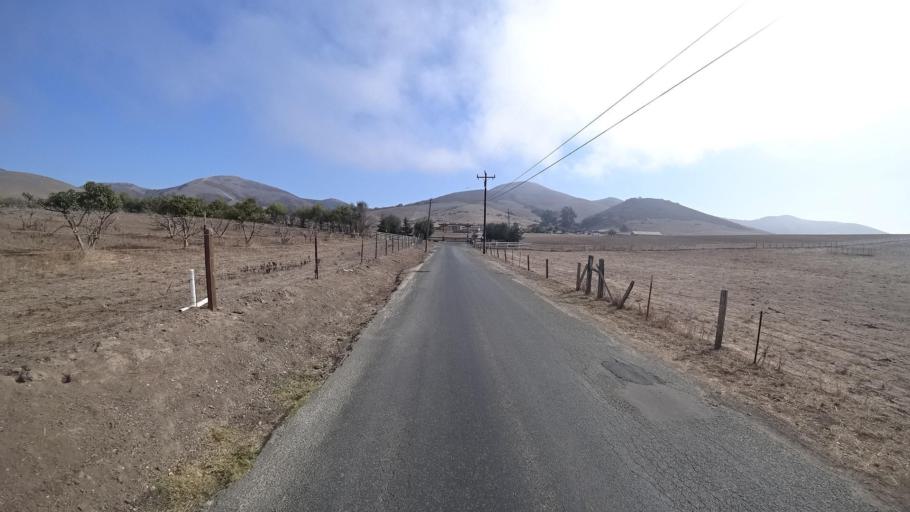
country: US
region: California
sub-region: Monterey County
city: Salinas
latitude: 36.7349
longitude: -121.5918
